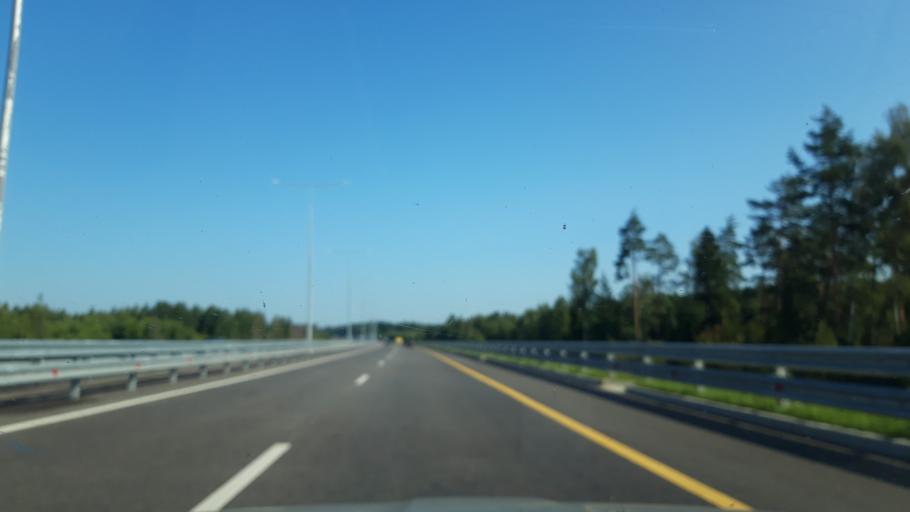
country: RU
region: Moskovskaya
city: Spas-Zaulok
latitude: 56.4734
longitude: 36.5403
